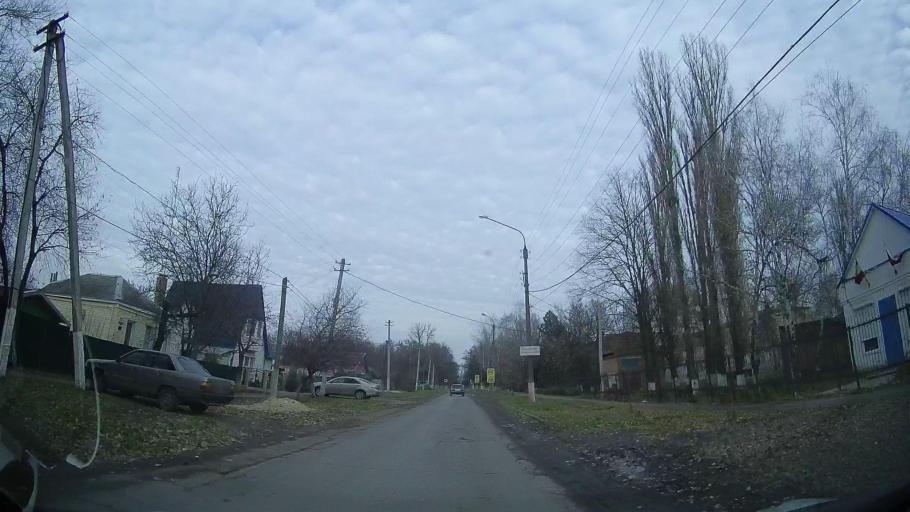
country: RU
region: Rostov
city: Zernograd
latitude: 46.8511
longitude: 40.3120
